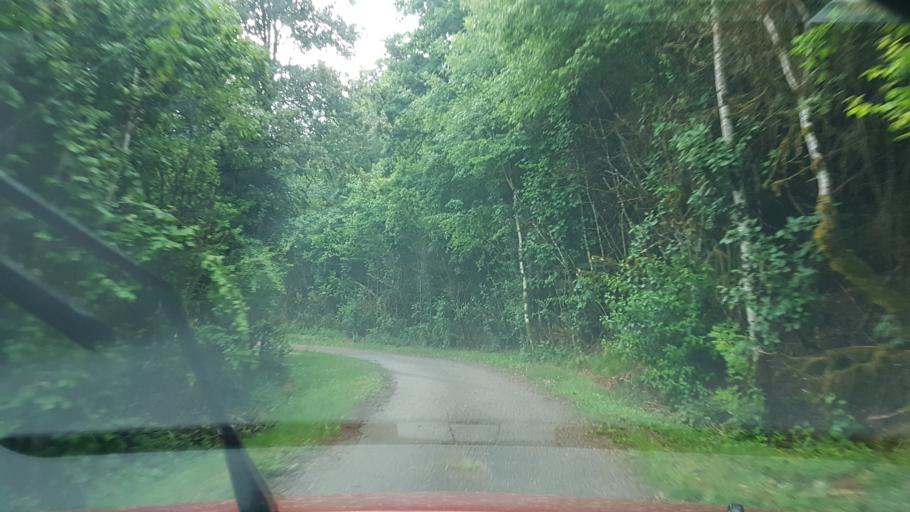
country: FR
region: Franche-Comte
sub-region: Departement du Jura
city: Clairvaux-les-Lacs
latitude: 46.5280
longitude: 5.7176
